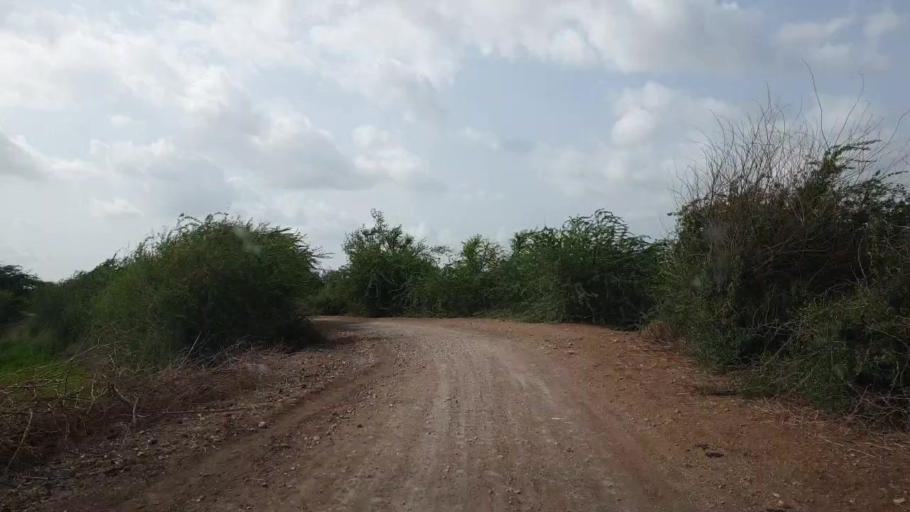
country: PK
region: Sindh
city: Kario
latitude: 24.6966
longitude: 68.6484
